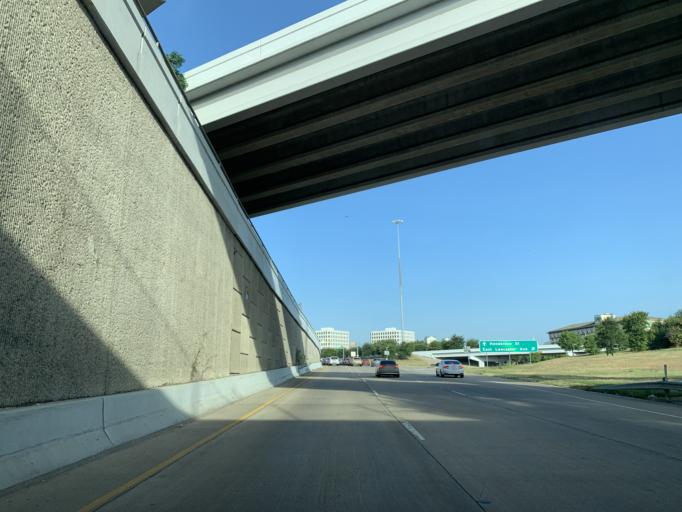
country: US
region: Texas
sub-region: Tarrant County
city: Fort Worth
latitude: 32.7450
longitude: -97.3357
